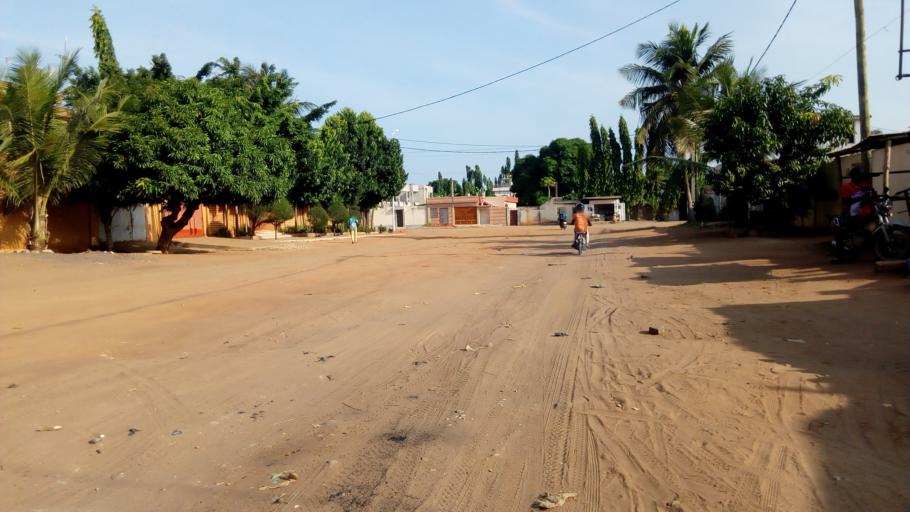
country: TG
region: Maritime
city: Lome
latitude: 6.1820
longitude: 1.1892
